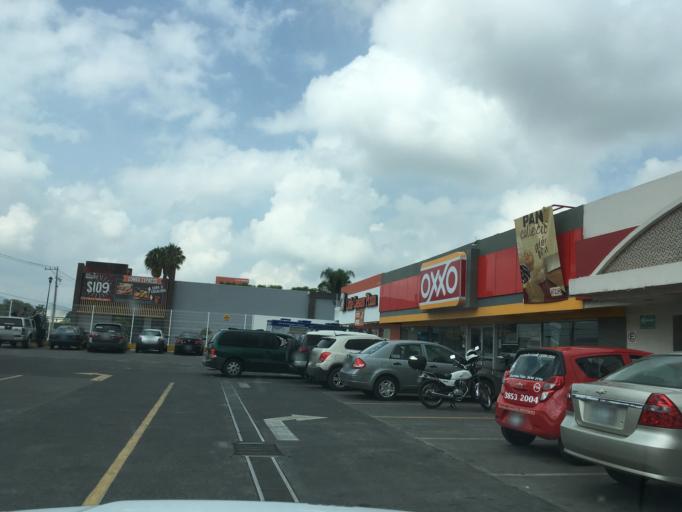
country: MX
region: Jalisco
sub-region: Tlajomulco de Zuniga
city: La Tijera
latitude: 20.5848
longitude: -103.4473
